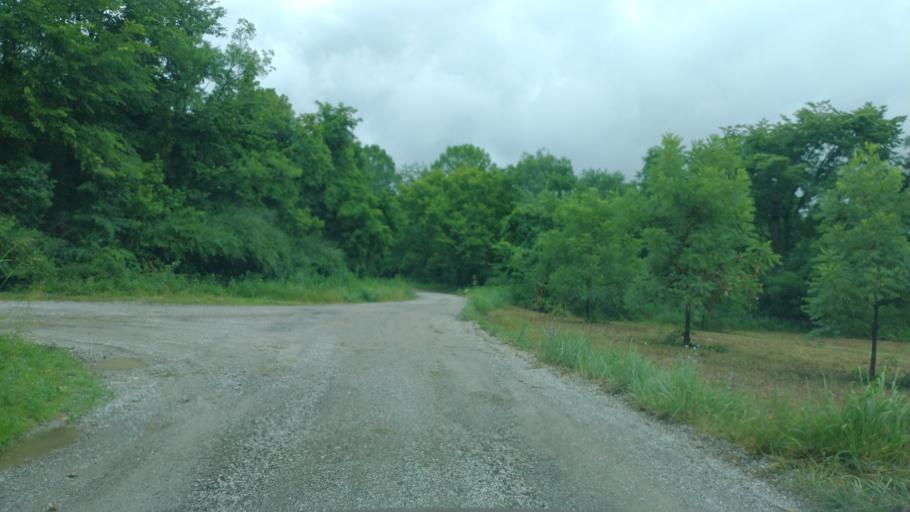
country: US
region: Ohio
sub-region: Meigs County
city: Middleport
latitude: 38.9312
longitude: -82.0693
